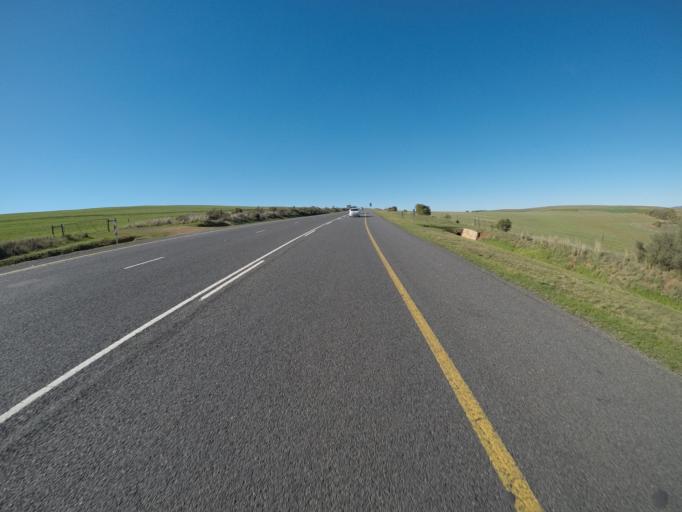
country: ZA
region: Western Cape
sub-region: Overberg District Municipality
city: Caledon
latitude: -34.2298
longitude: 19.2664
